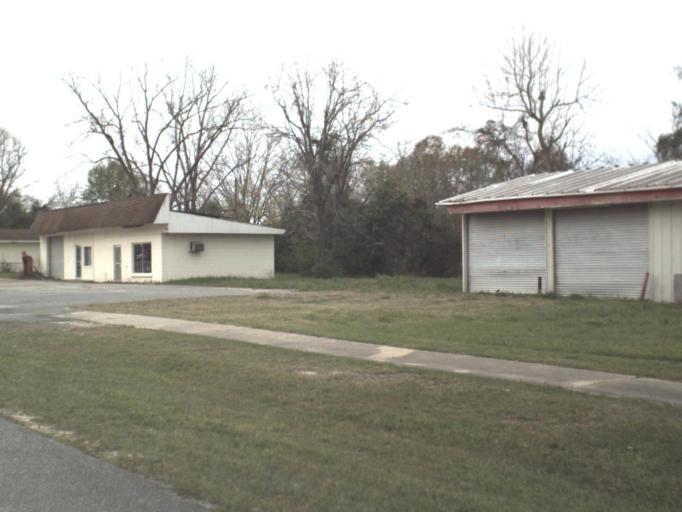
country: US
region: Alabama
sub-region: Geneva County
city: Hartford
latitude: 30.9859
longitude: -85.6464
